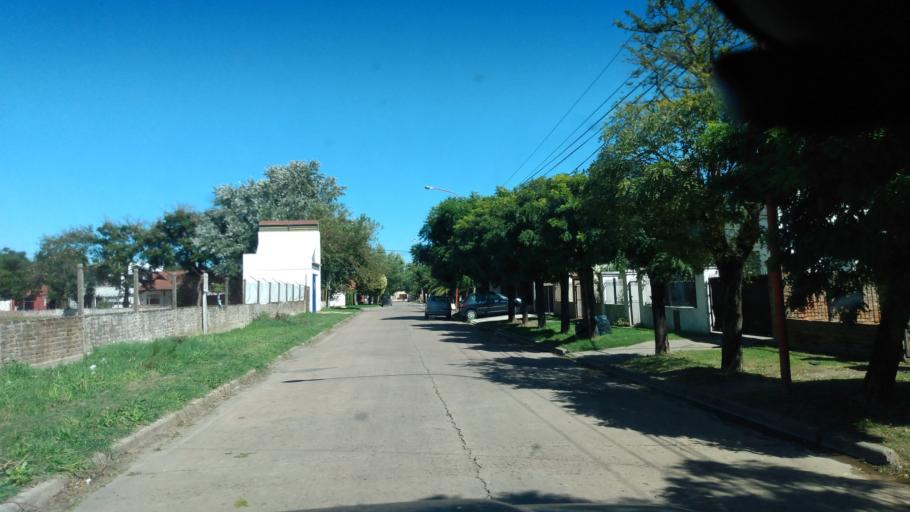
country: AR
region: Buenos Aires
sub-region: Partido de Lujan
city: Lujan
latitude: -34.5777
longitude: -59.1100
